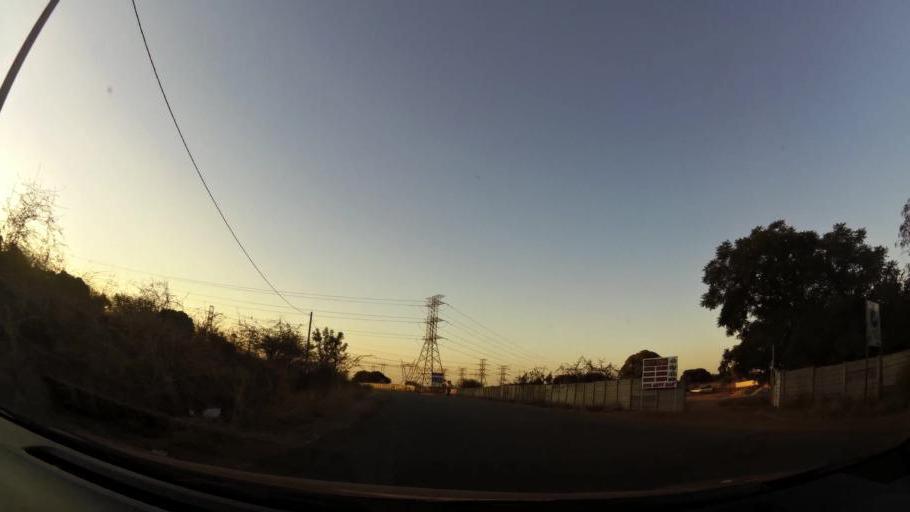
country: ZA
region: North-West
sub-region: Bojanala Platinum District Municipality
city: Rustenburg
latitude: -25.6330
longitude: 27.2021
